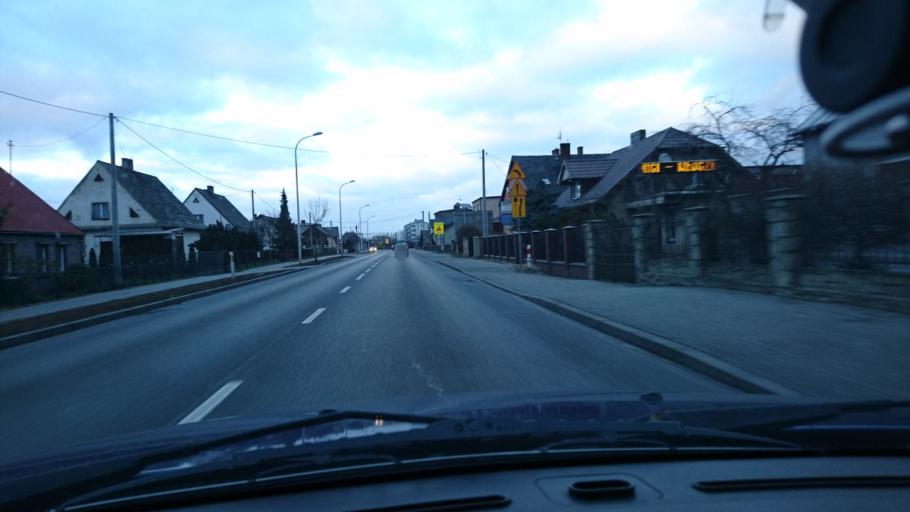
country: PL
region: Greater Poland Voivodeship
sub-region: Powiat kepinski
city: Kepno
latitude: 51.2954
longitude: 17.9965
